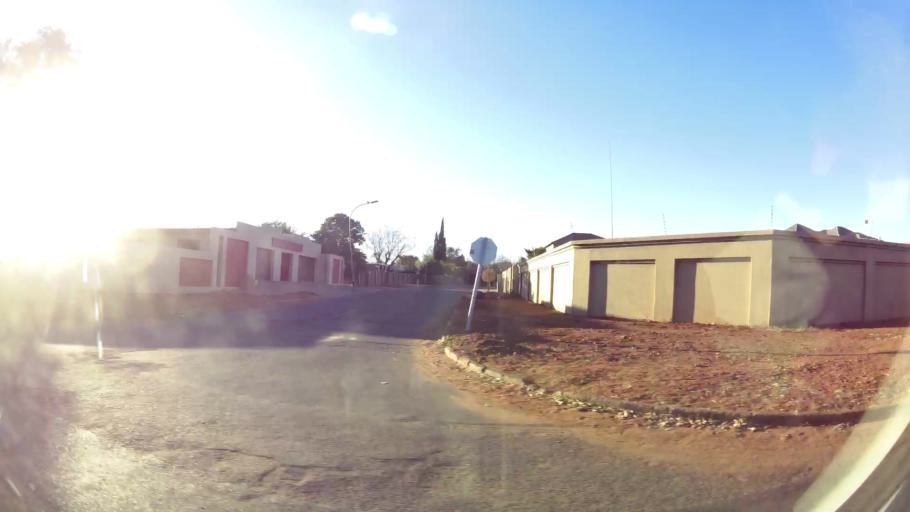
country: ZA
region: Northern Cape
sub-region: Frances Baard District Municipality
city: Kimberley
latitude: -28.7559
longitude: 24.7399
